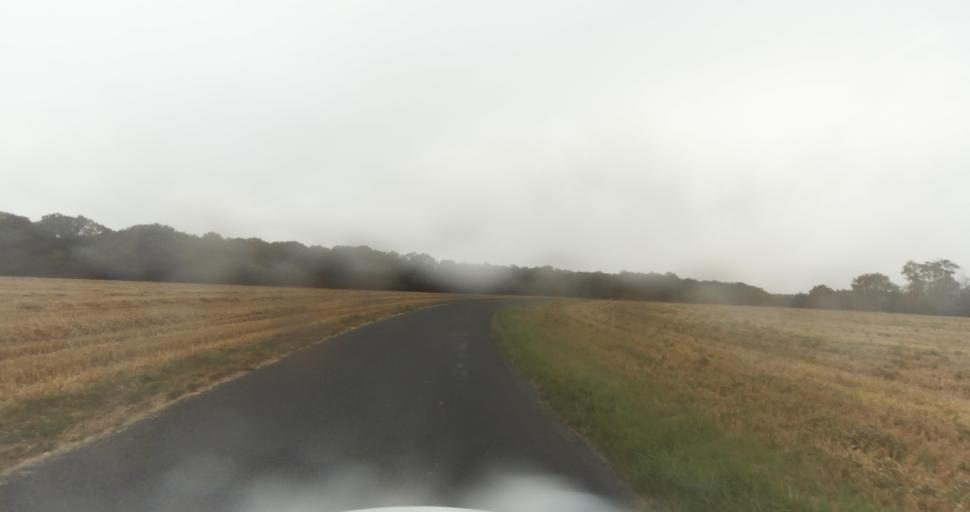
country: FR
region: Centre
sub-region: Departement d'Eure-et-Loir
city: Saint-Remy-sur-Avre
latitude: 48.7747
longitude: 1.2448
